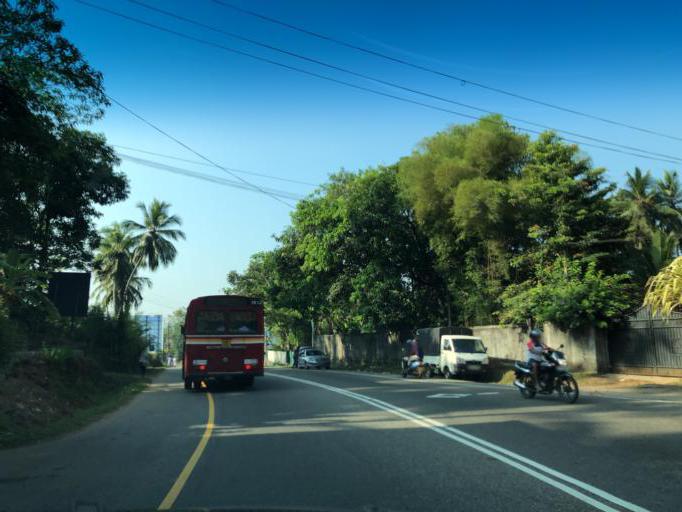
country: LK
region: Western
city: Horana South
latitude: 6.7295
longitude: 80.0981
